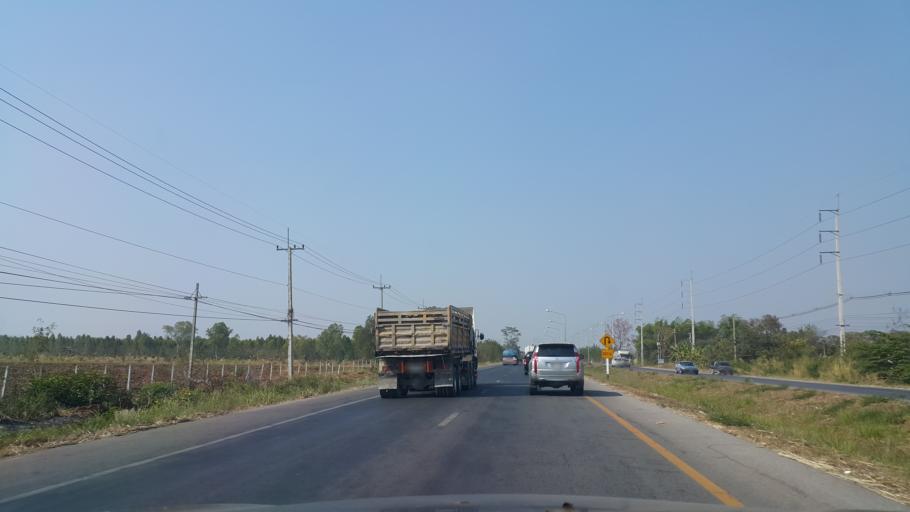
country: TH
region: Chaiyaphum
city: Phu Khiao
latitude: 16.4360
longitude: 102.1270
